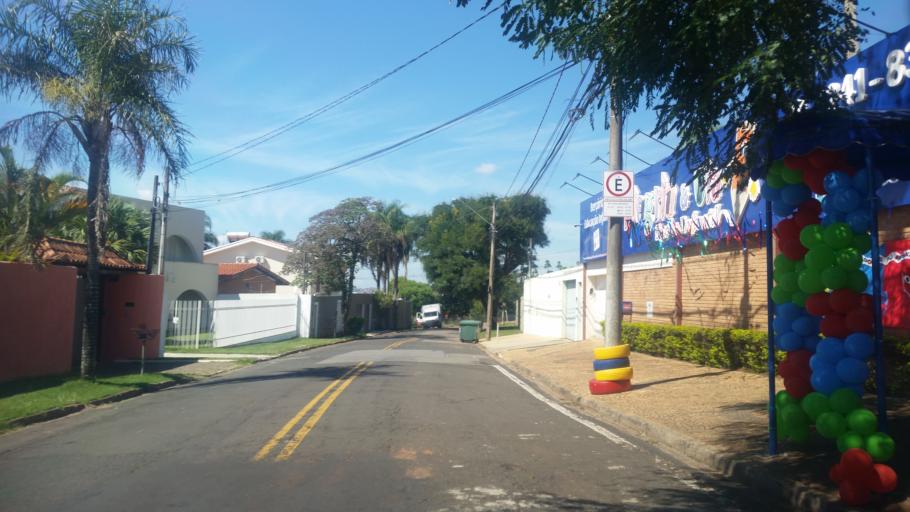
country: BR
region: Sao Paulo
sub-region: Campinas
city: Campinas
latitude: -22.8647
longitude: -47.0511
